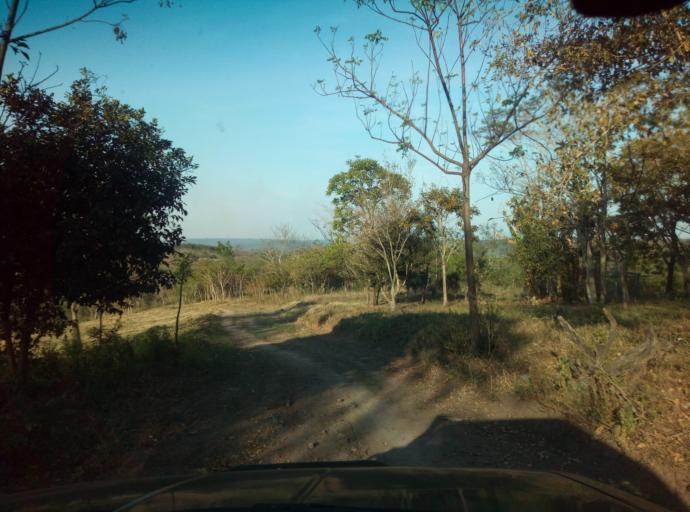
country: PY
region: Caaguazu
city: Doctor Cecilio Baez
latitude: -25.2006
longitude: -56.1298
